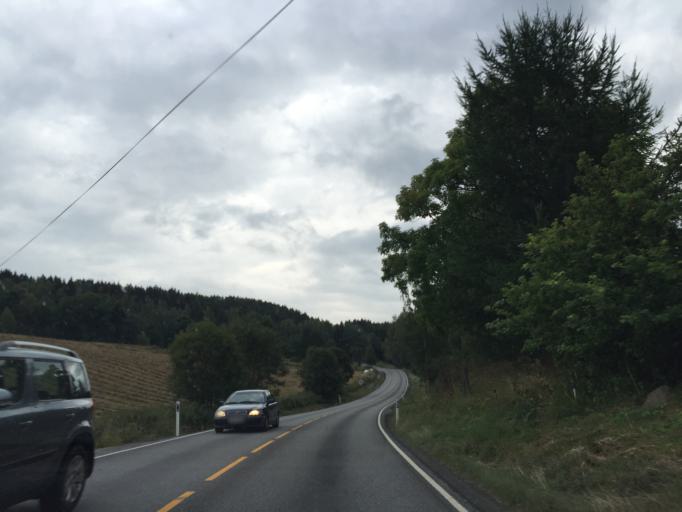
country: NO
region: Hedmark
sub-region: Loten
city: Loten
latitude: 60.6825
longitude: 11.3489
